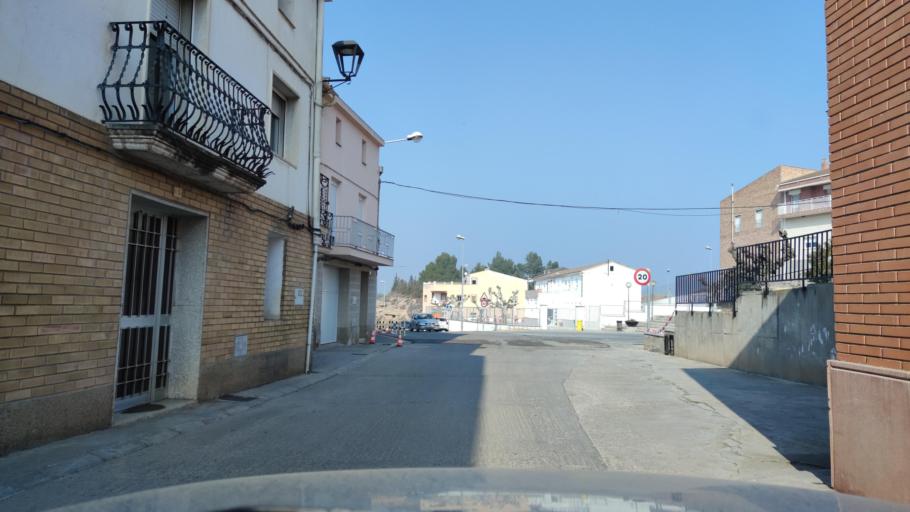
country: ES
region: Catalonia
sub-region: Provincia de Lleida
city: Sunyer
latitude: 41.5602
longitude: 0.5890
